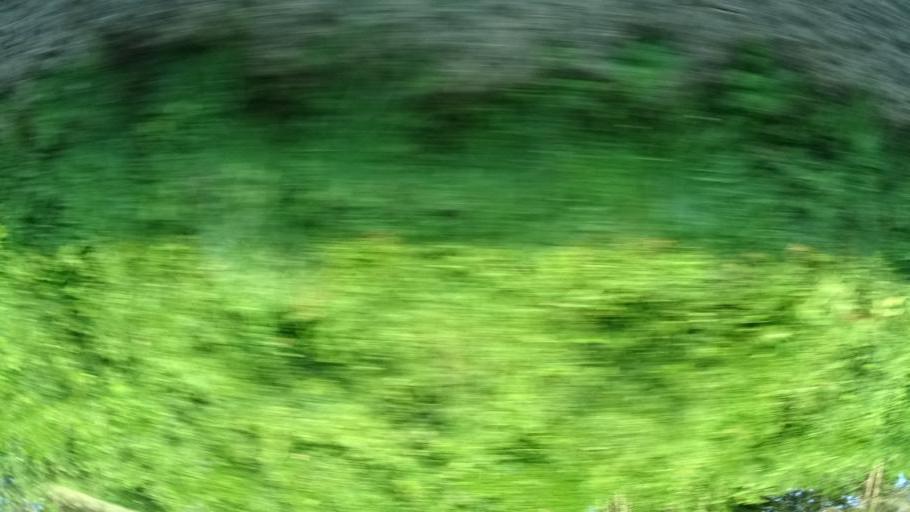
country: JP
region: Ibaraki
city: Funaishikawa
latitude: 36.4499
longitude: 140.5499
